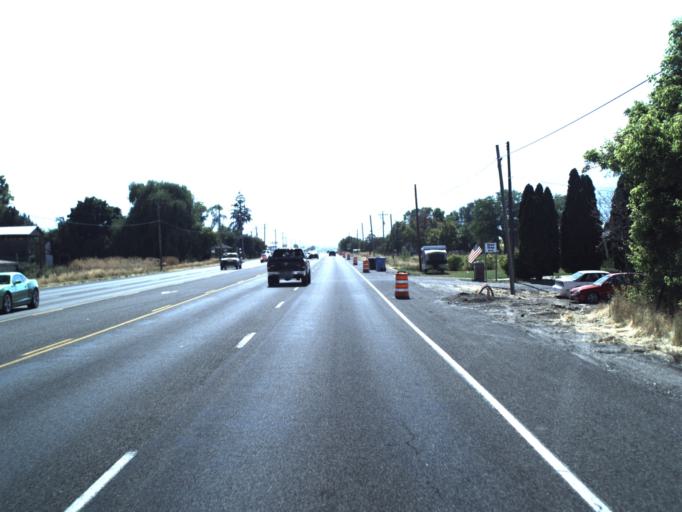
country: US
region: Utah
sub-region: Cache County
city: Nibley
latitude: 41.6793
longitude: -111.8794
